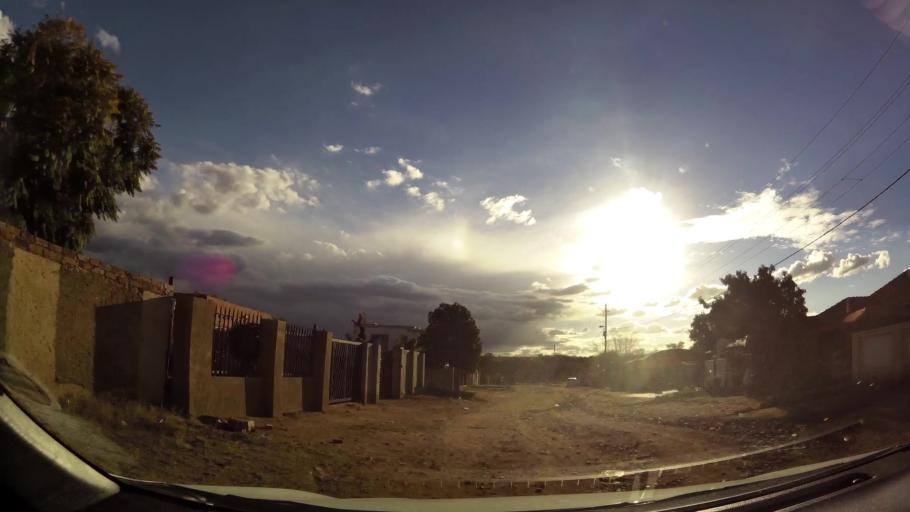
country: ZA
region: Limpopo
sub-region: Capricorn District Municipality
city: Polokwane
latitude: -23.9113
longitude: 29.4248
